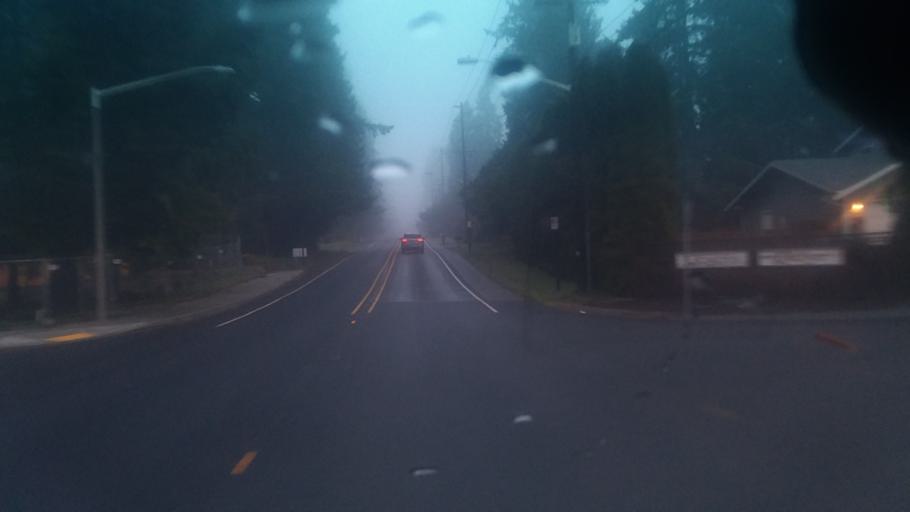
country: US
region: Washington
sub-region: Pierce County
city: South Hill
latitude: 47.1425
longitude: -122.3148
